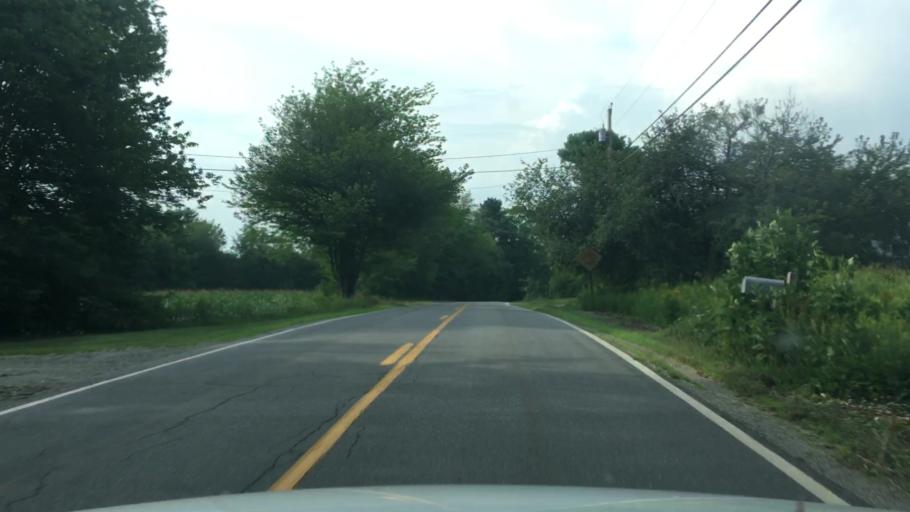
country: US
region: Maine
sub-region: Lincoln County
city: Waldoboro
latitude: 44.1599
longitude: -69.3774
